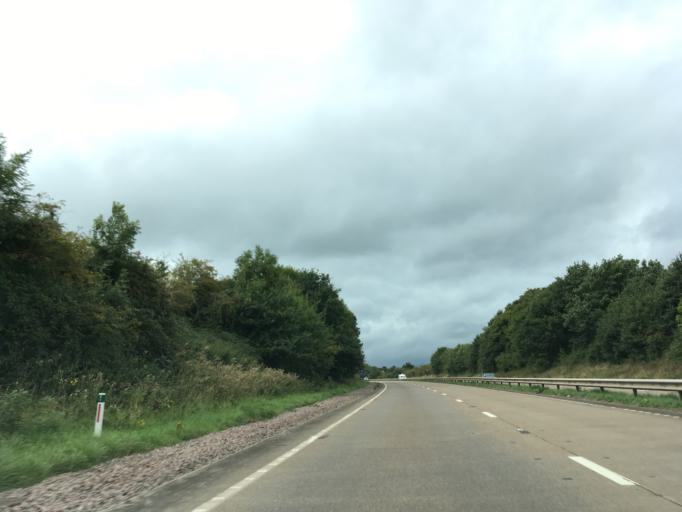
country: GB
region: Wales
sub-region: Monmouthshire
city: Llanarth
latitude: 51.7730
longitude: -2.8731
